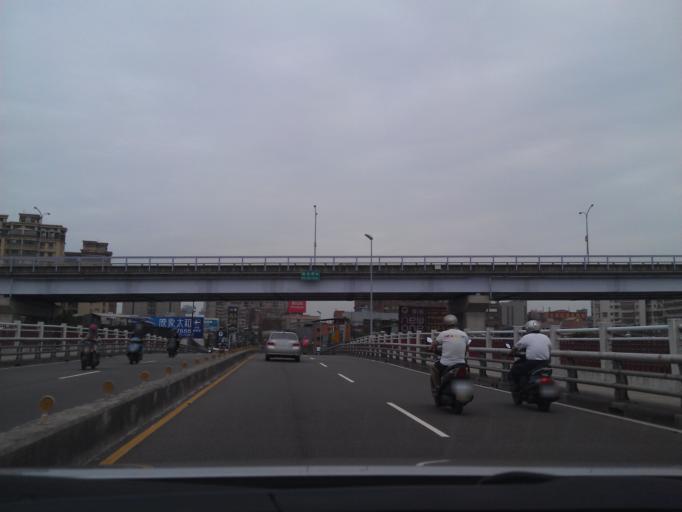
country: TW
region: Taipei
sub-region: Taipei
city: Banqiao
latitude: 25.0227
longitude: 121.4865
